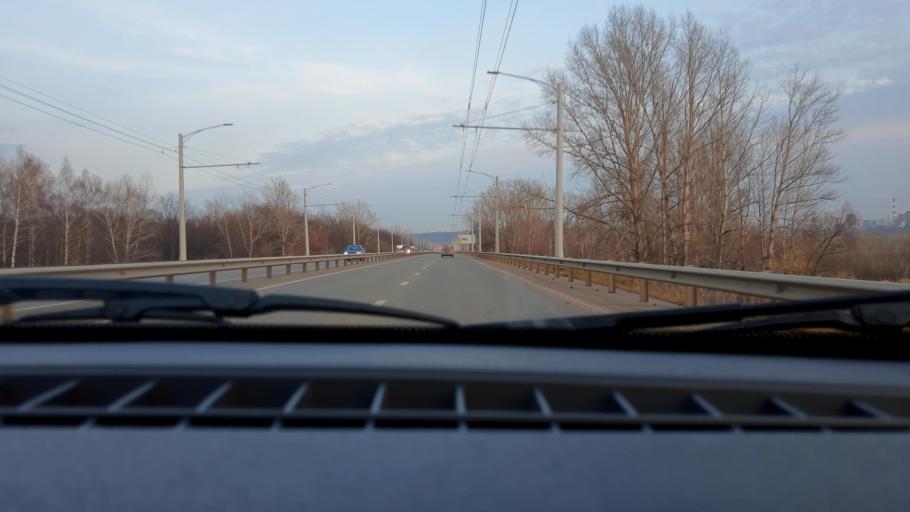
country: RU
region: Bashkortostan
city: Ufa
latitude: 54.7676
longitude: 55.9247
